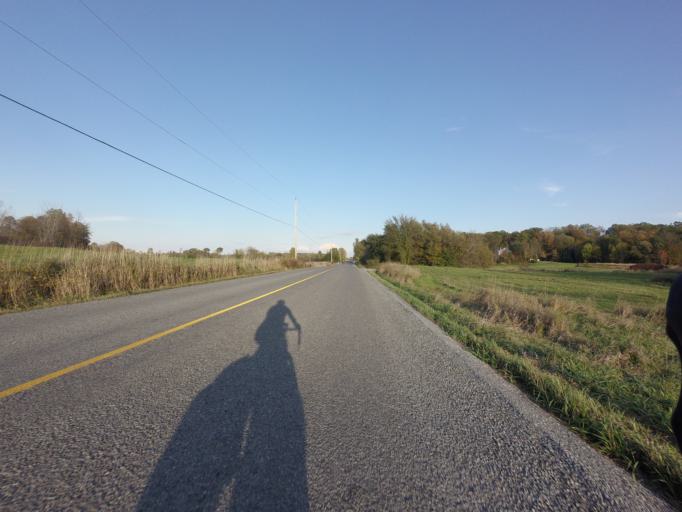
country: CA
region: Ontario
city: Kingston
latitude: 44.3757
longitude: -76.3870
